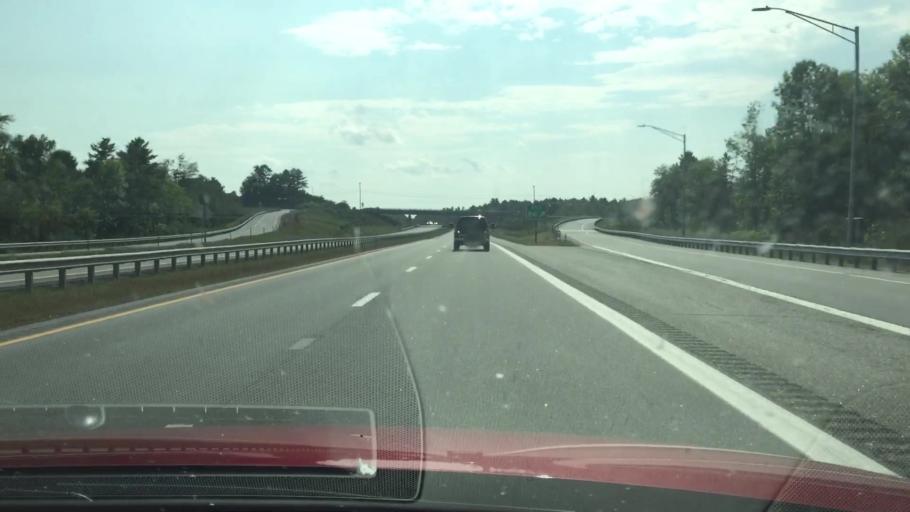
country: US
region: Maine
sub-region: Androscoggin County
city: Sabattus
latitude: 44.1033
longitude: -70.0819
